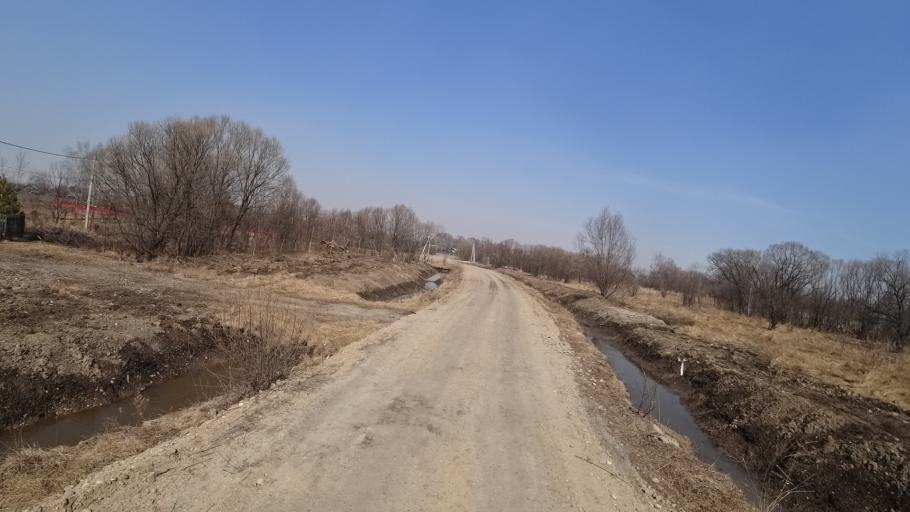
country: RU
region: Amur
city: Novobureyskiy
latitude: 49.7766
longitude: 129.8486
